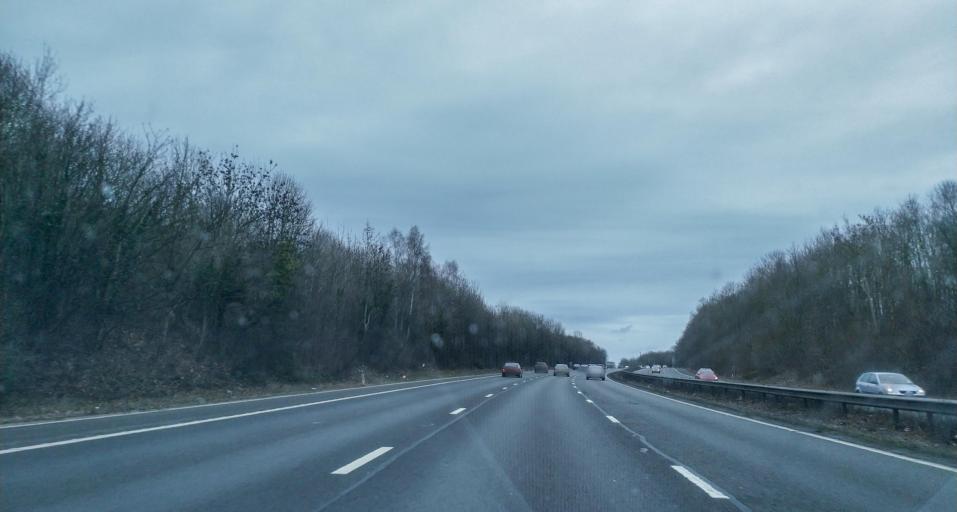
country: GB
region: England
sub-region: Buckinghamshire
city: High Wycombe
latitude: 51.6141
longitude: -0.7454
